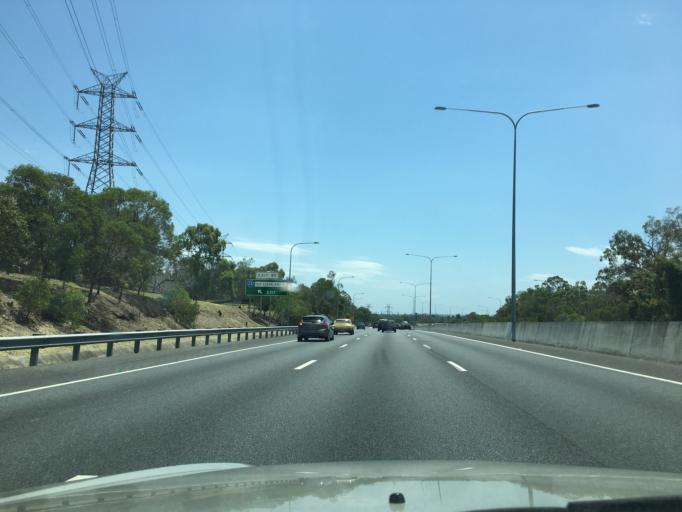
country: AU
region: Queensland
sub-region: Brisbane
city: Belmont
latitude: -27.5090
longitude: 153.1253
